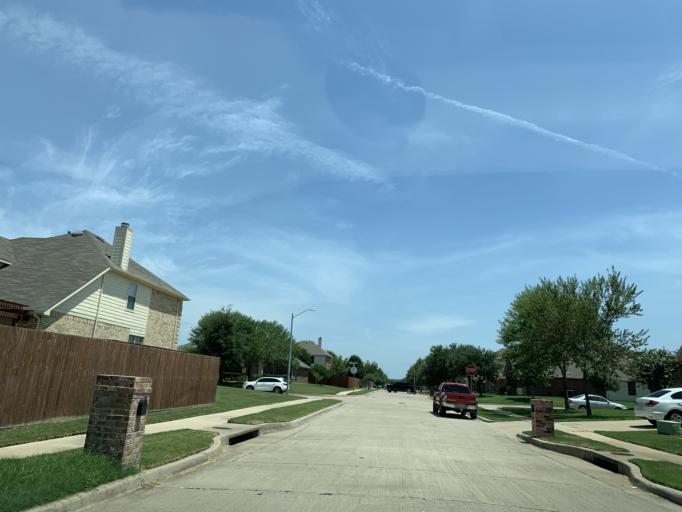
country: US
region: Texas
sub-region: Dallas County
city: Cedar Hill
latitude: 32.6461
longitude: -97.0218
